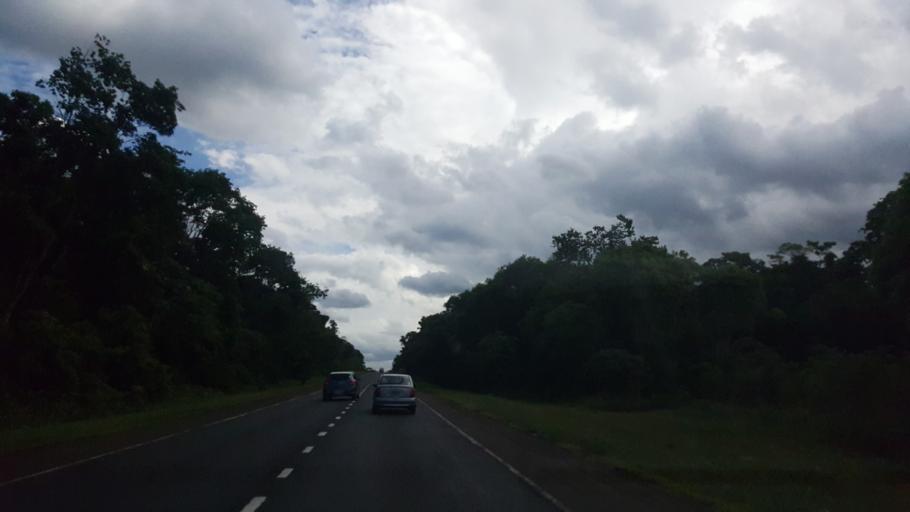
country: AR
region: Misiones
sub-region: Departamento de Iguazu
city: Puerto Iguazu
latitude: -25.7103
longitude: -54.5176
